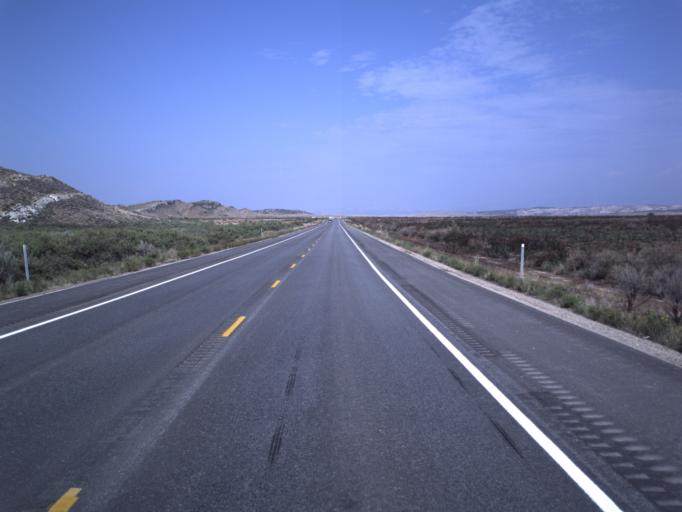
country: US
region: Utah
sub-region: Uintah County
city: Naples
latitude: 40.2882
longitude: -109.1497
